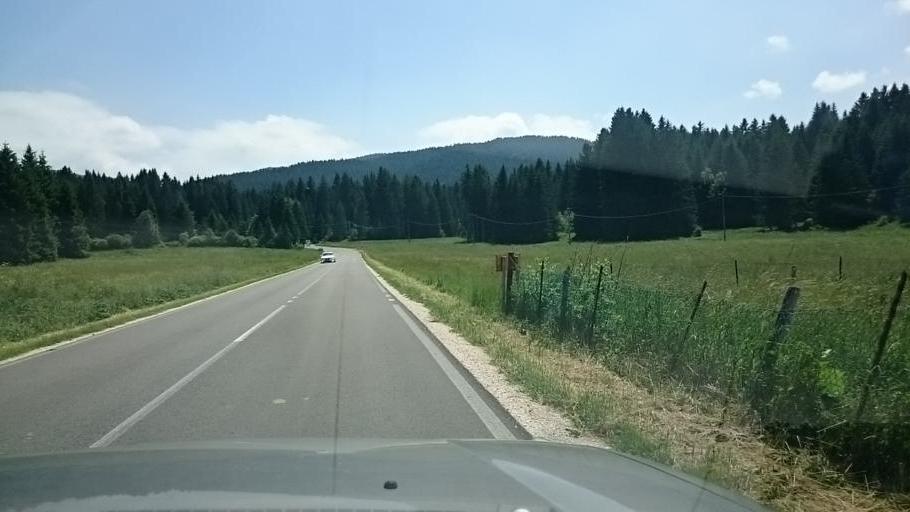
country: IT
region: Veneto
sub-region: Provincia di Vicenza
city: Gallio
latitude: 45.8558
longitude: 11.5491
